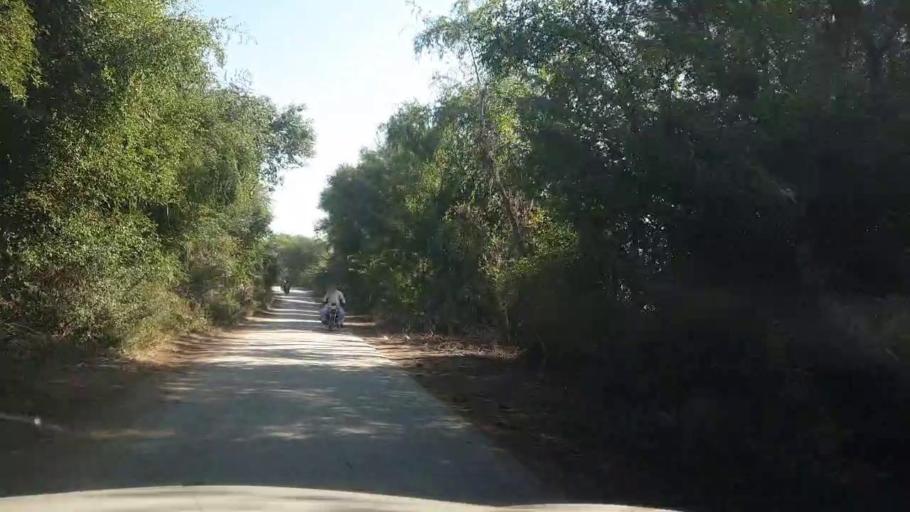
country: PK
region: Sindh
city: Bhan
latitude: 26.5420
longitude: 67.7035
